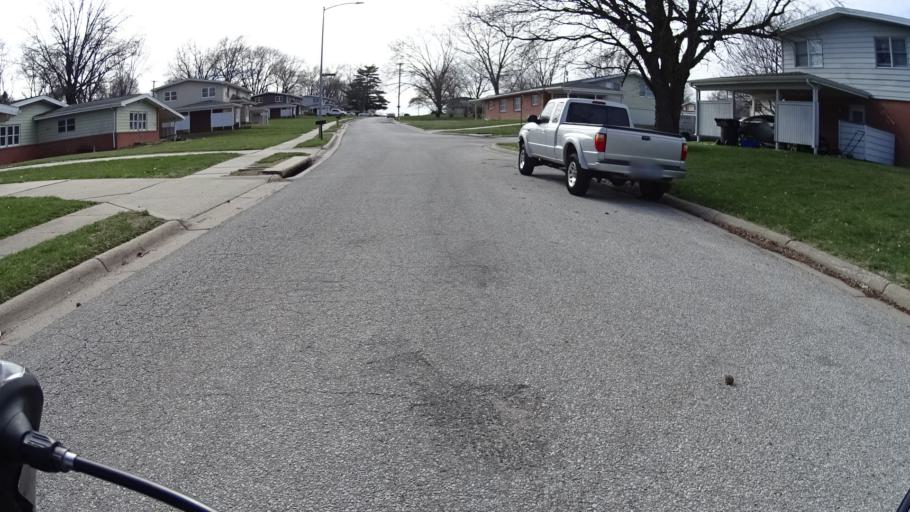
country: US
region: Nebraska
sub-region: Sarpy County
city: Offutt Air Force Base
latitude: 41.1187
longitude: -95.9612
